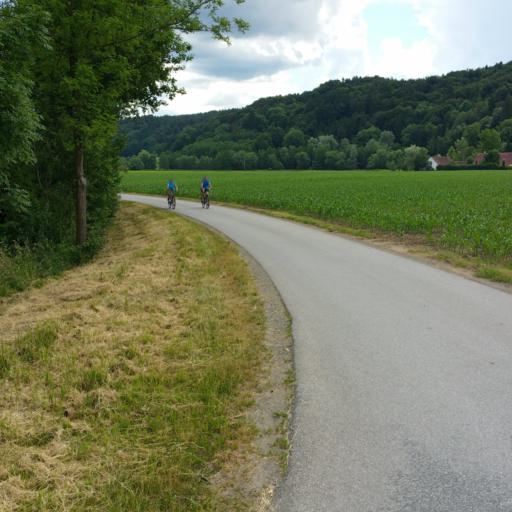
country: AT
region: Styria
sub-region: Politischer Bezirk Leibnitz
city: Gleinstatten
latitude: 46.7405
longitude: 15.3407
